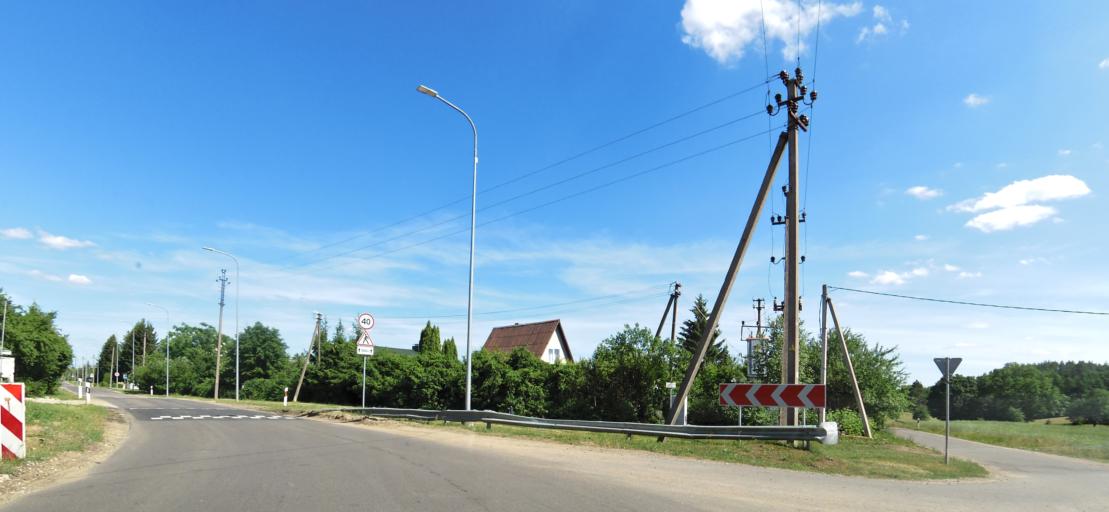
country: LT
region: Vilnius County
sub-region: Vilnius
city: Fabijoniskes
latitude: 54.8000
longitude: 25.3332
